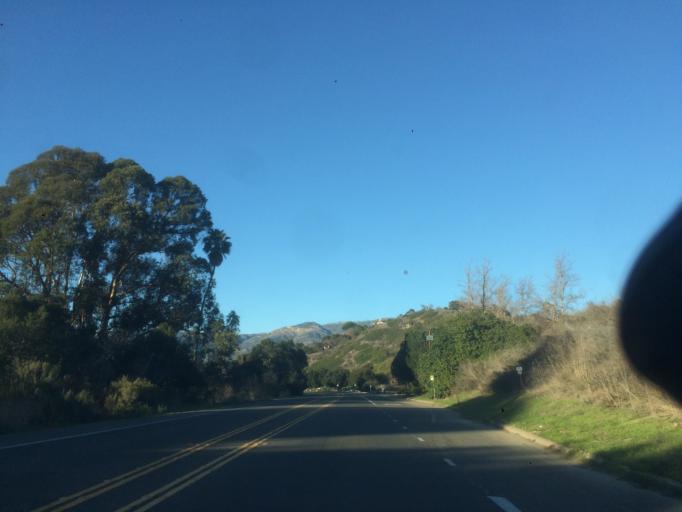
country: US
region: California
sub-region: Santa Barbara County
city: Santa Barbara
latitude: 34.4119
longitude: -119.7403
